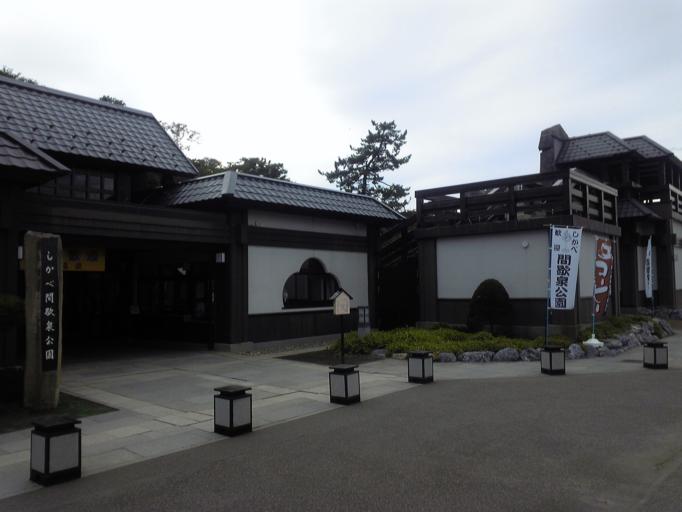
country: JP
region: Hokkaido
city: Nanae
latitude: 42.0289
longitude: 140.8307
